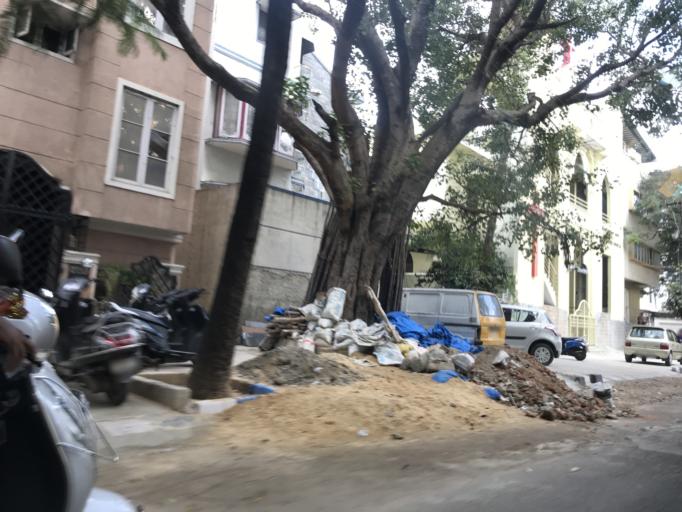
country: IN
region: Karnataka
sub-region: Bangalore Urban
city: Bangalore
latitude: 12.9578
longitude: 77.5640
